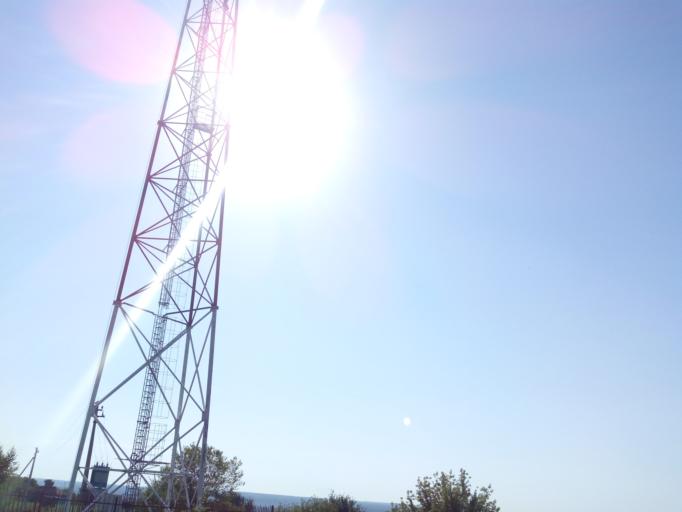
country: RU
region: Tambov
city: Zherdevka
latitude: 51.7311
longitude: 41.4608
